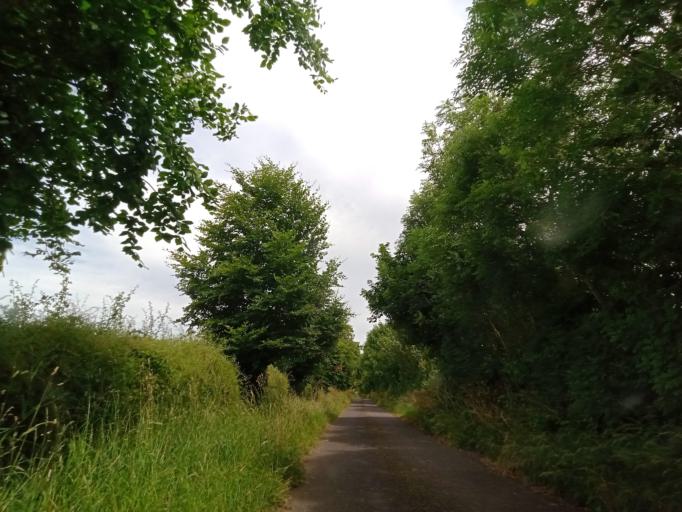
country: IE
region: Leinster
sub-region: Kilkenny
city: Thomastown
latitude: 52.5835
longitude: -7.1232
